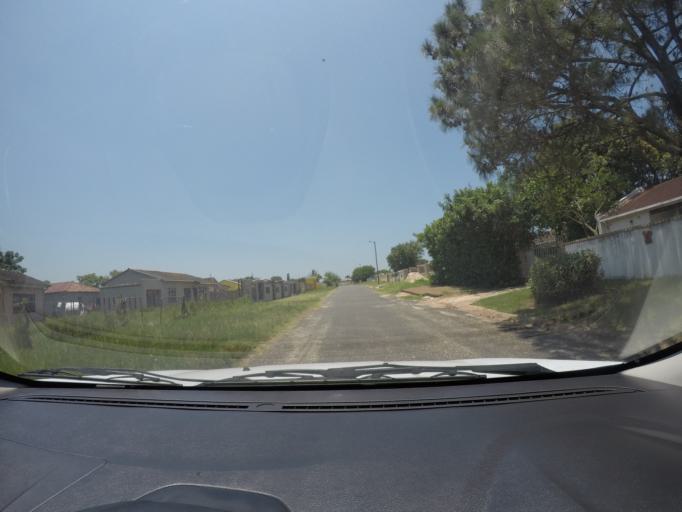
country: ZA
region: KwaZulu-Natal
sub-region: uThungulu District Municipality
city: eSikhawini
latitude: -28.8852
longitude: 31.8961
